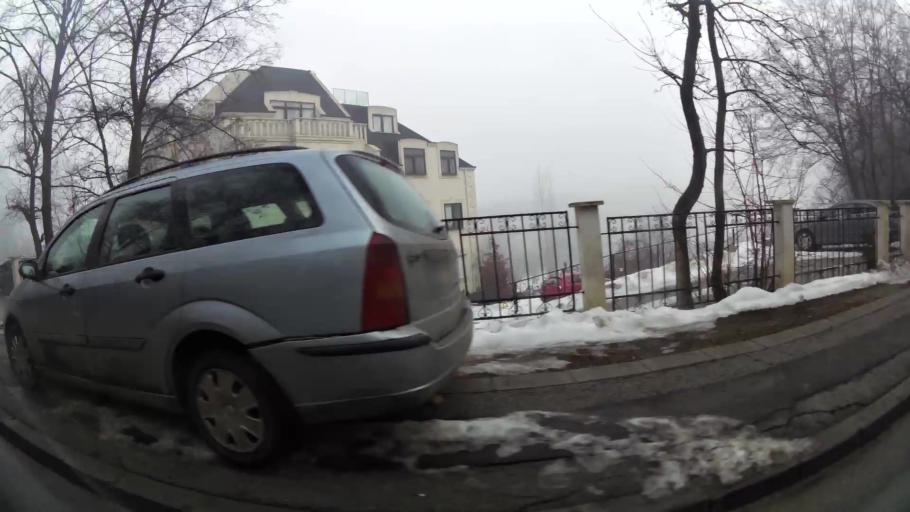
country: BG
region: Sofia-Capital
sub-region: Stolichna Obshtina
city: Sofia
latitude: 42.6531
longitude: 23.2529
